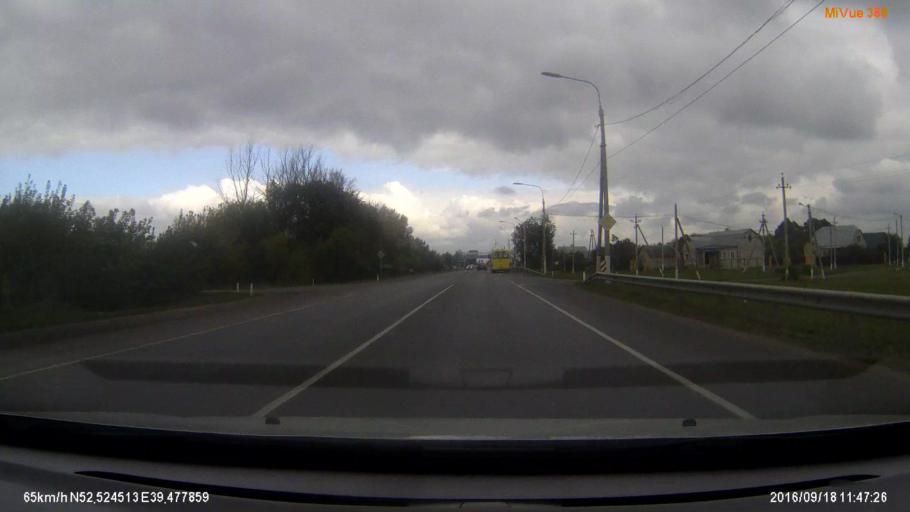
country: RU
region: Lipetsk
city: Syrskoye
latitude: 52.5244
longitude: 39.4777
